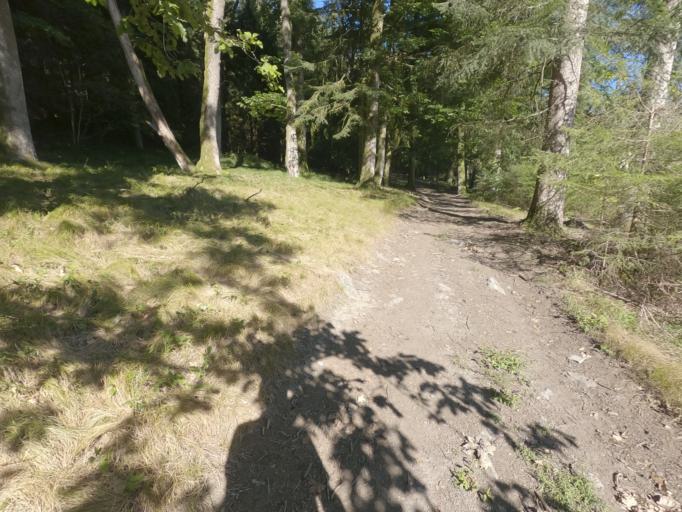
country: DE
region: Bavaria
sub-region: Lower Bavaria
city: Schaufling
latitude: 48.8255
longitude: 13.0250
